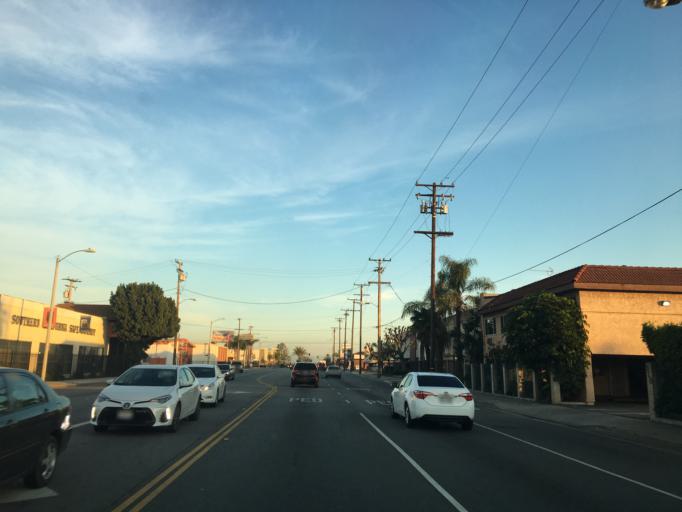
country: US
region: California
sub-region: Los Angeles County
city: Montebello
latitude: 33.9932
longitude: -118.1147
